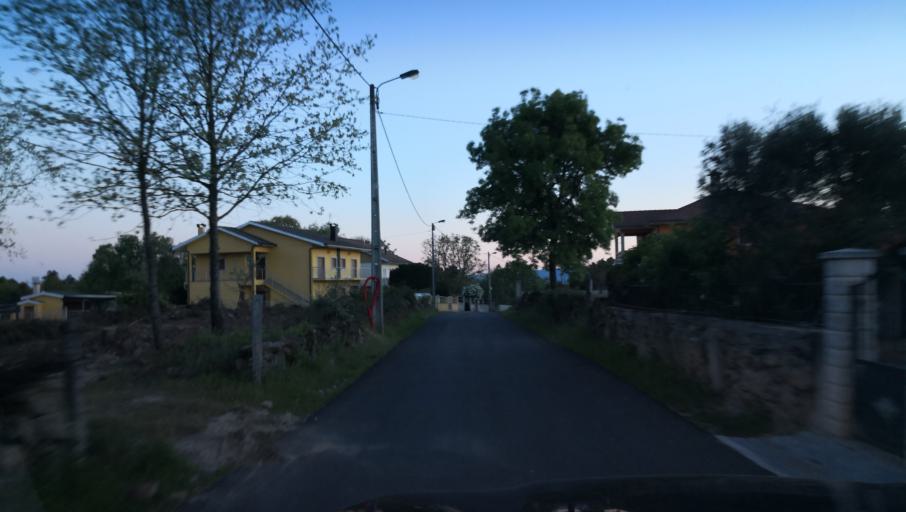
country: PT
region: Vila Real
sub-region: Vila Real
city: Vila Real
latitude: 41.2982
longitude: -7.6729
